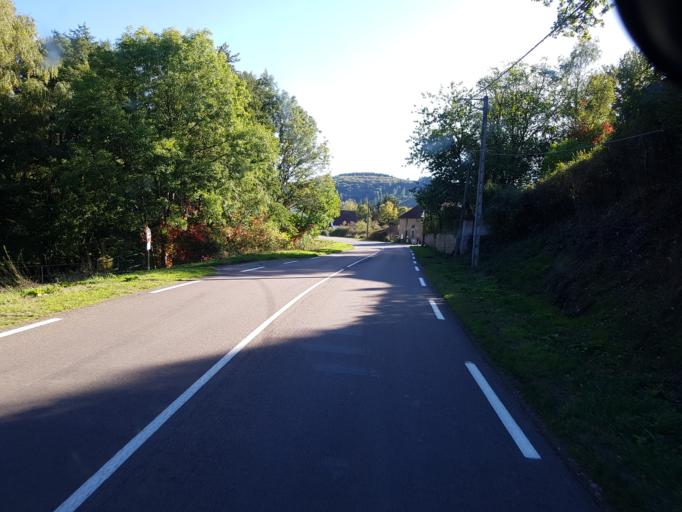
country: FR
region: Bourgogne
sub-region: Departement de Saone-et-Loire
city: Autun
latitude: 47.1031
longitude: 4.2308
